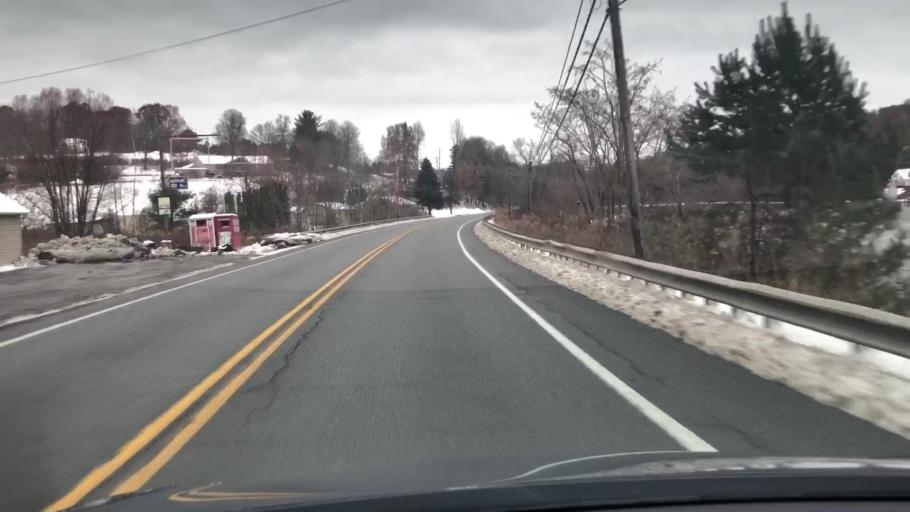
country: US
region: Pennsylvania
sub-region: Clearfield County
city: Treasure Lake
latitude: 41.1587
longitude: -78.6676
